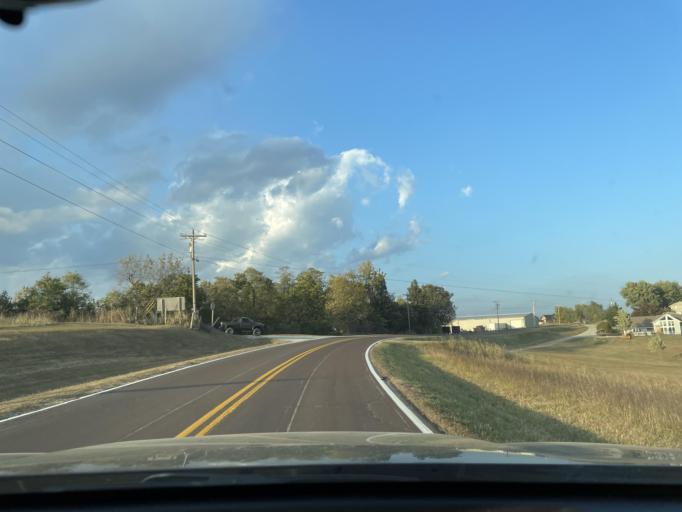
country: US
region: Missouri
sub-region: Andrew County
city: Savannah
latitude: 39.9153
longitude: -94.8760
